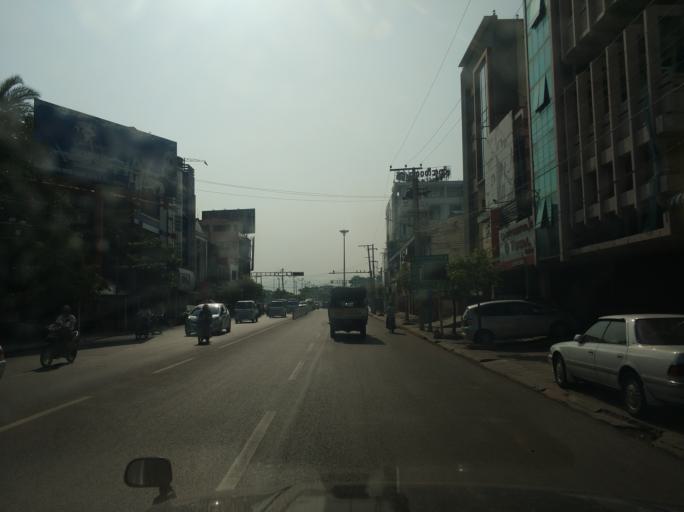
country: MM
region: Mandalay
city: Mandalay
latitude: 21.9832
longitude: 96.0832
